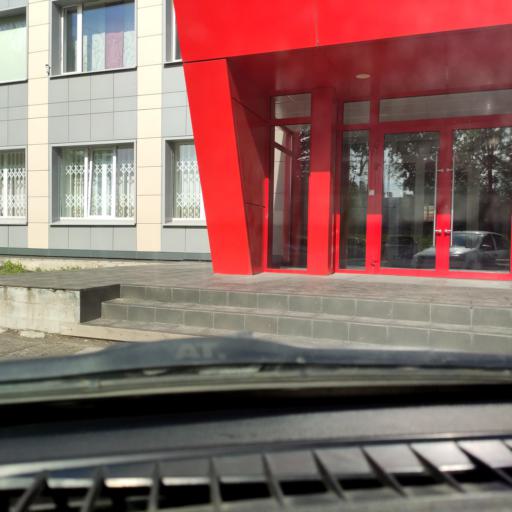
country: RU
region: Samara
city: Tol'yatti
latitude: 53.5140
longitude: 49.4620
